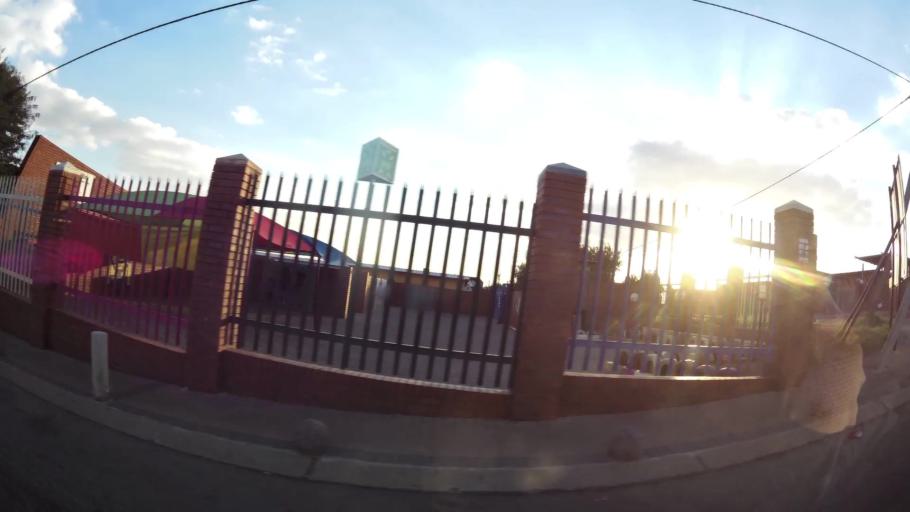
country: ZA
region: Gauteng
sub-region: West Rand District Municipality
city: Krugersdorp
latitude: -26.0812
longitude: 27.7530
